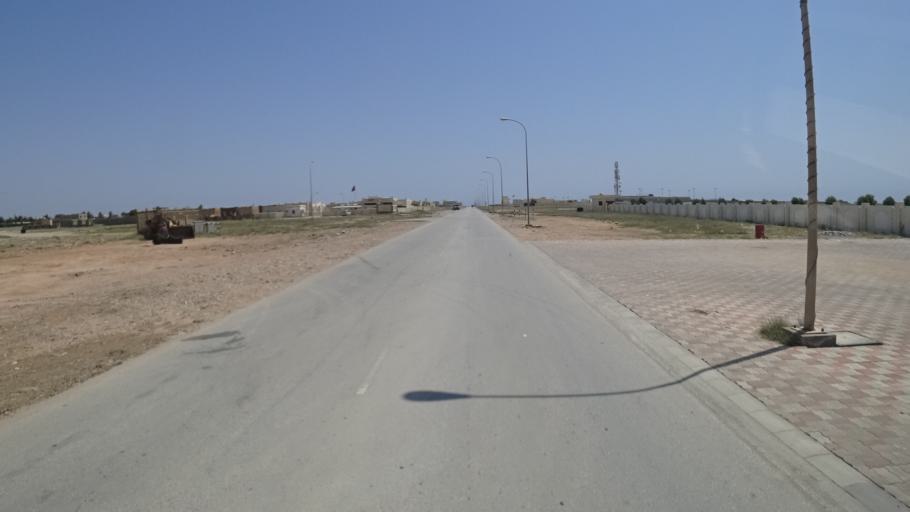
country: OM
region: Zufar
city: Salalah
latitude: 16.9875
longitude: 54.6971
